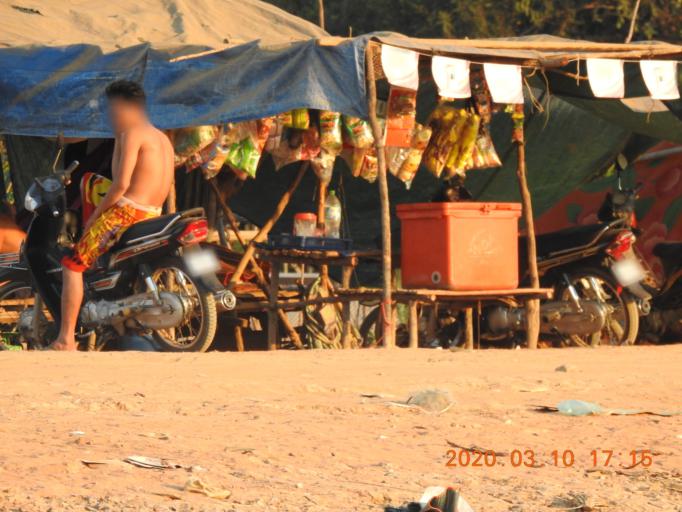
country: KH
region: Siem Reap
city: Siem Reap
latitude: 13.2569
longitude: 103.8230
